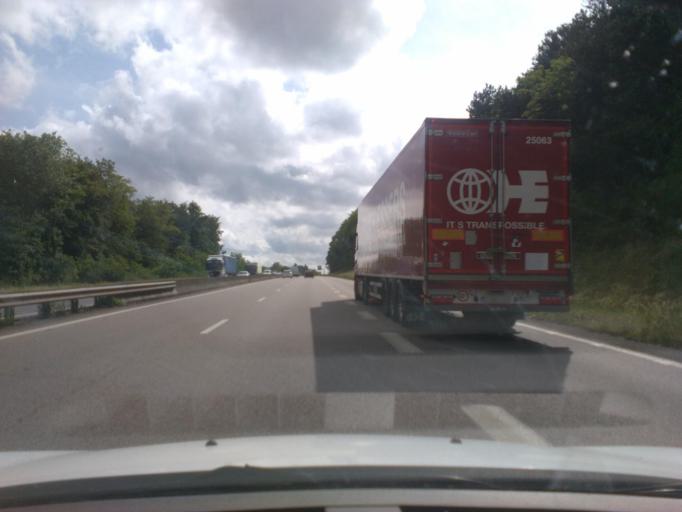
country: FR
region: Lorraine
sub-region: Departement de Meurthe-et-Moselle
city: Maxeville
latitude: 48.7106
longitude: 6.1450
